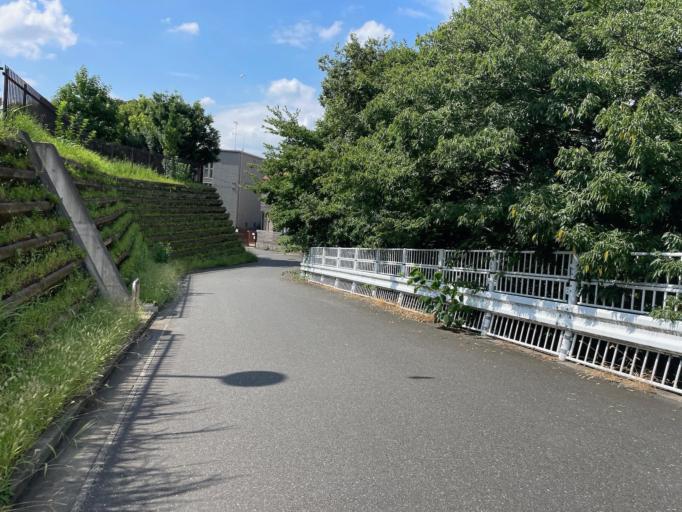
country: JP
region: Saitama
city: Wako
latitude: 35.7911
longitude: 139.6195
